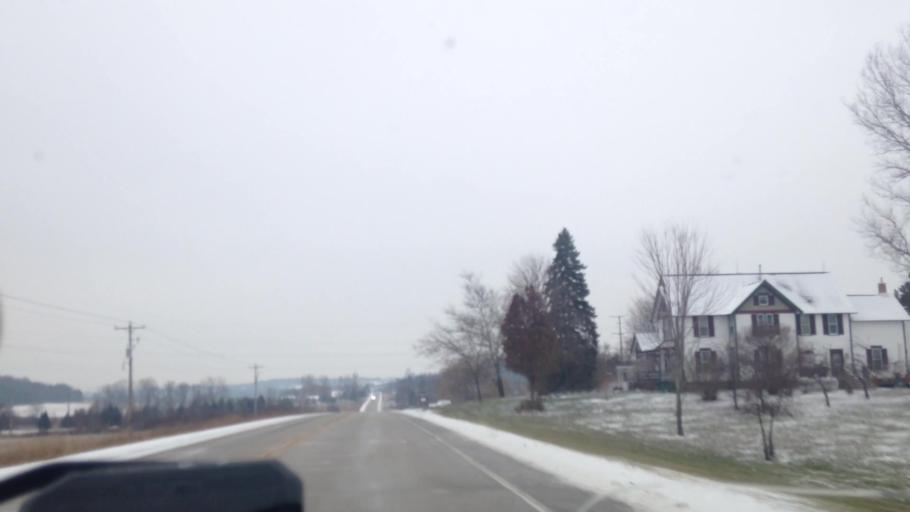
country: US
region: Wisconsin
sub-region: Dodge County
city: Hustisford
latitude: 43.3000
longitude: -88.5185
